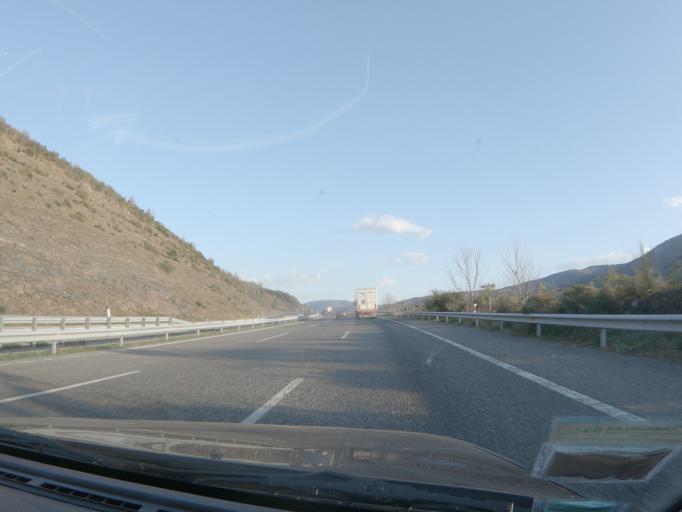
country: ES
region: Galicia
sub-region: Provincia de Lugo
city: San Roman
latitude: 42.7751
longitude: -7.0962
